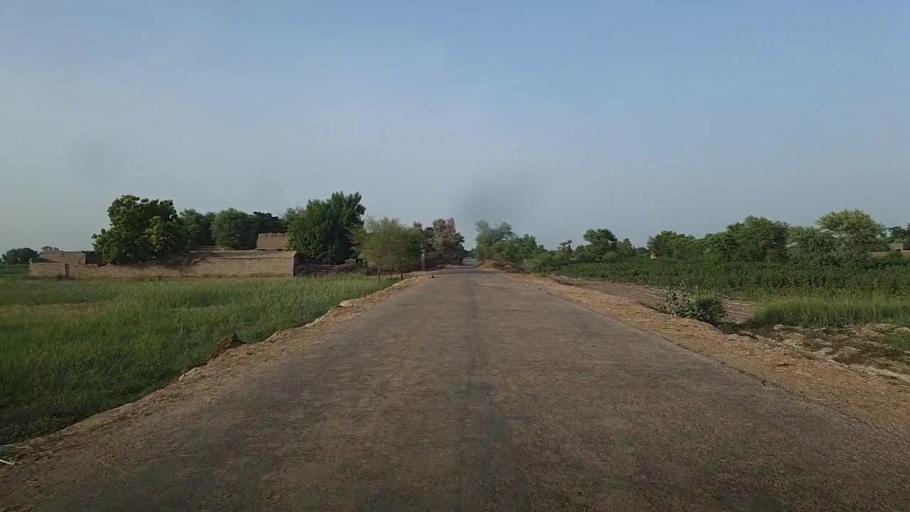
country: PK
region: Sindh
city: Ubauro
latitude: 28.1257
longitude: 69.8296
